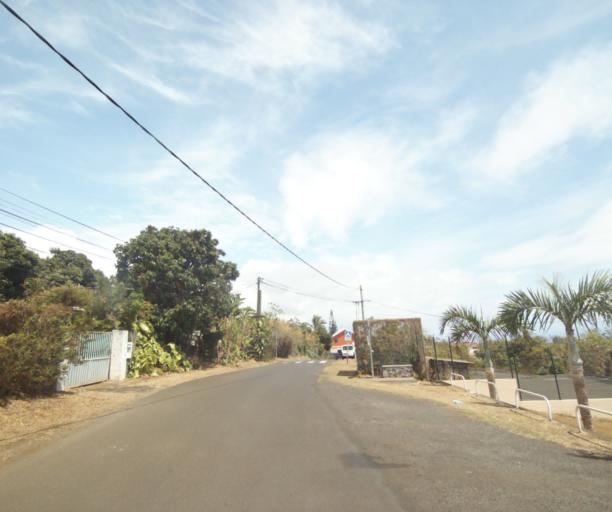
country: RE
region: Reunion
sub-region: Reunion
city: Trois-Bassins
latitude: -21.0978
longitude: 55.2774
